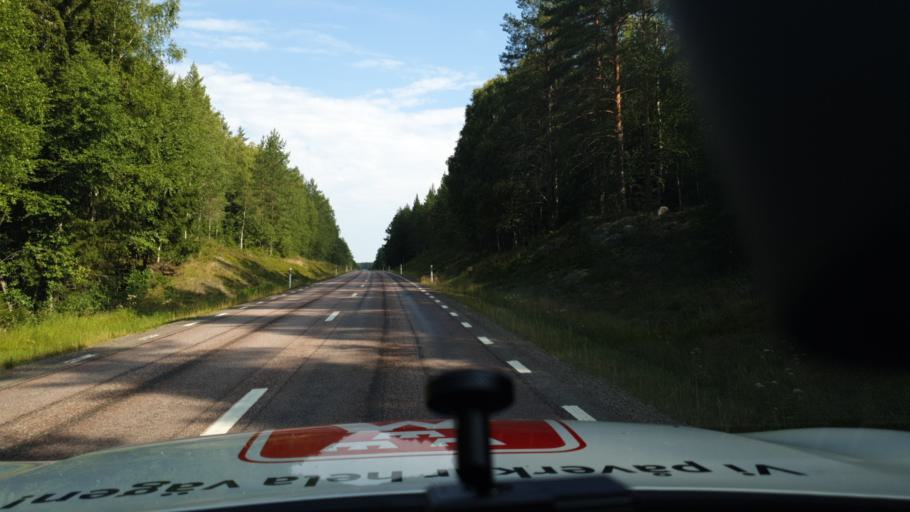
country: SE
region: Vaermland
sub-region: Hagfors Kommun
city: Ekshaerad
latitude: 60.4590
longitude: 13.2962
